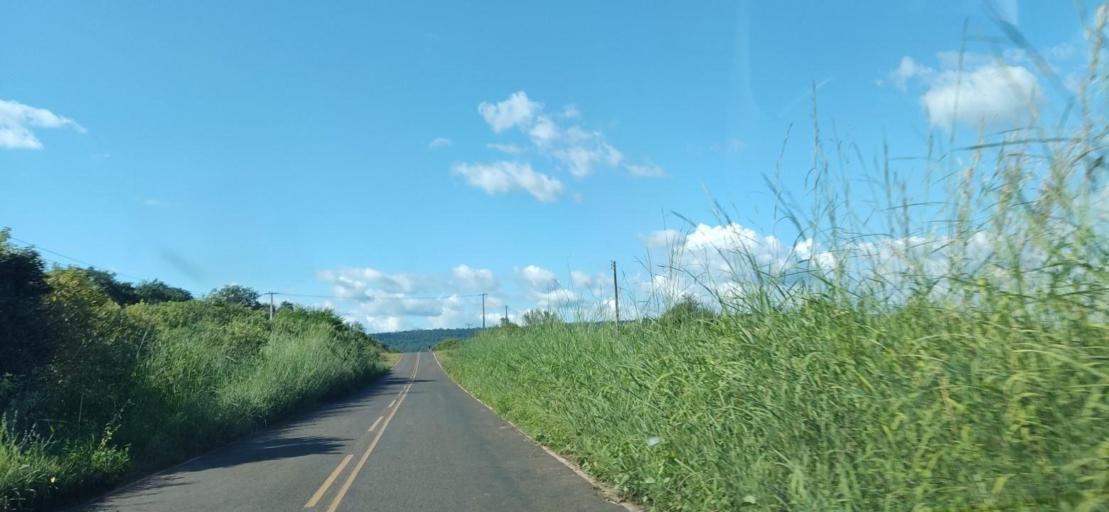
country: BR
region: Piaui
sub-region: Valenca Do Piaui
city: Valenca do Piaui
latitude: -6.1796
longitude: -41.8202
